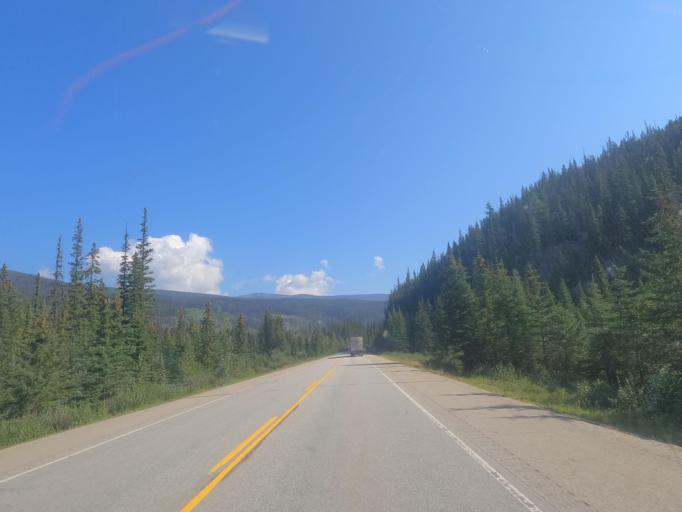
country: CA
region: Alberta
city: Jasper Park Lodge
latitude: 52.8845
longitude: -118.4849
